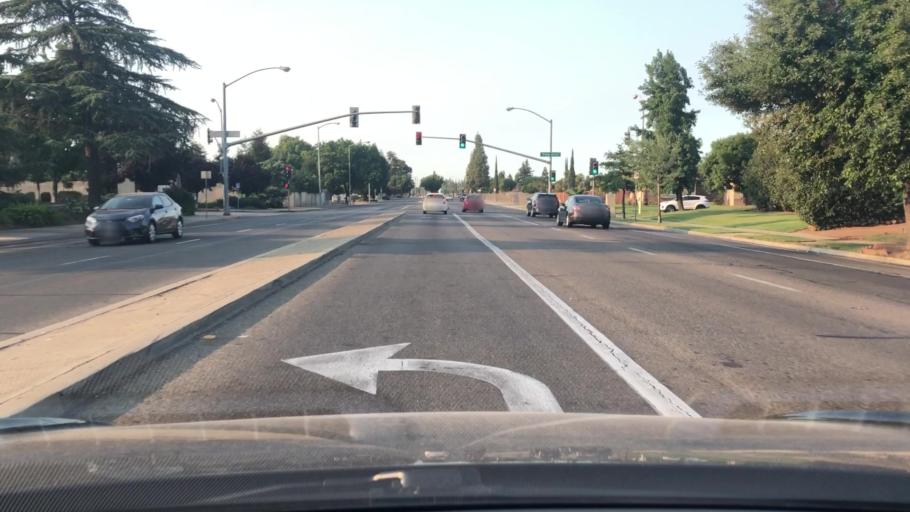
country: US
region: California
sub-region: Fresno County
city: Clovis
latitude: 36.8353
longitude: -119.7542
